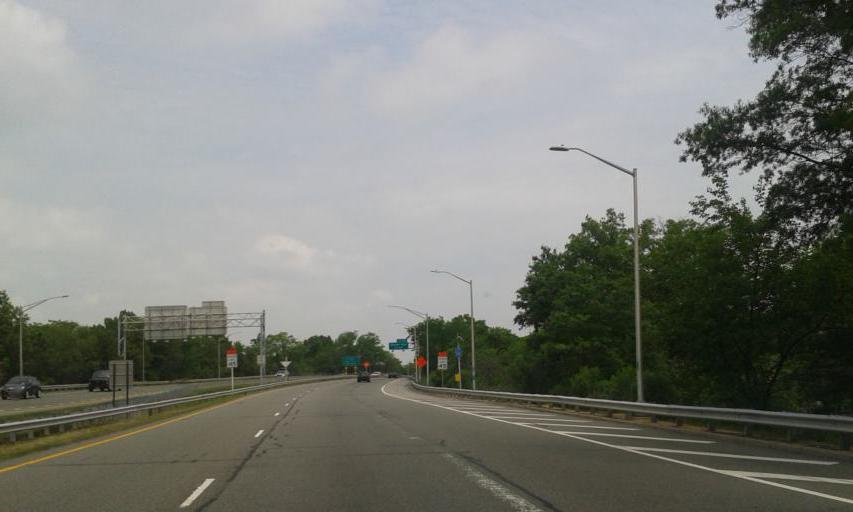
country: US
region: New York
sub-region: Richmond County
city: Bloomfield
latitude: 40.6153
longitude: -74.1528
